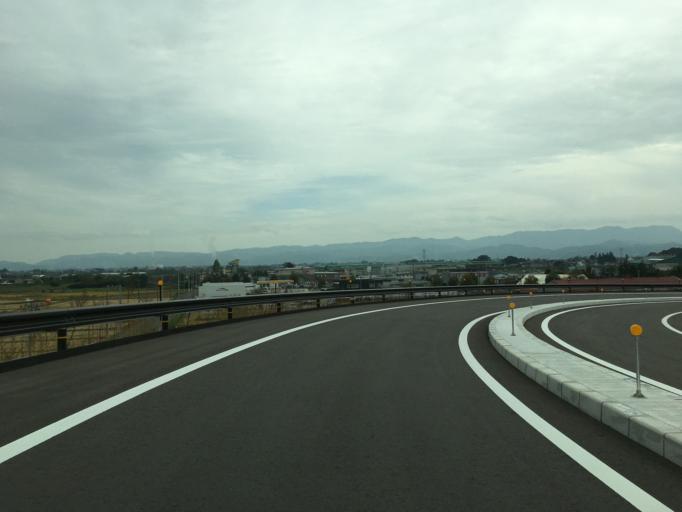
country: JP
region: Fukushima
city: Hobaramachi
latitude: 37.8295
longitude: 140.5101
